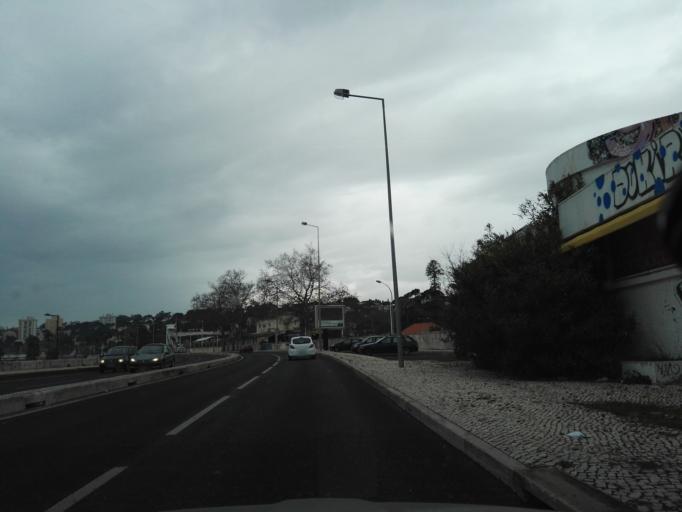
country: PT
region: Lisbon
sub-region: Oeiras
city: Terrugem
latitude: 38.6982
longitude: -9.2727
